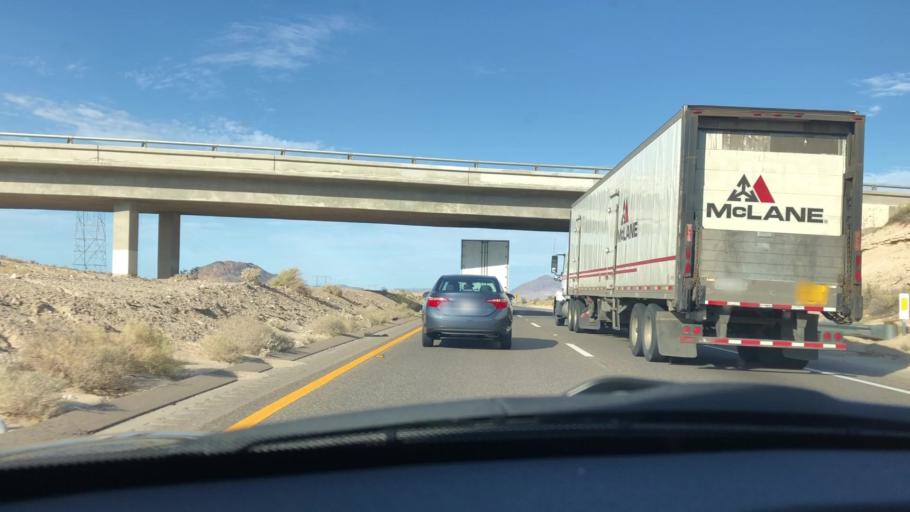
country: US
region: California
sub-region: San Bernardino County
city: Fort Irwin
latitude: 35.0107
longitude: -116.5316
